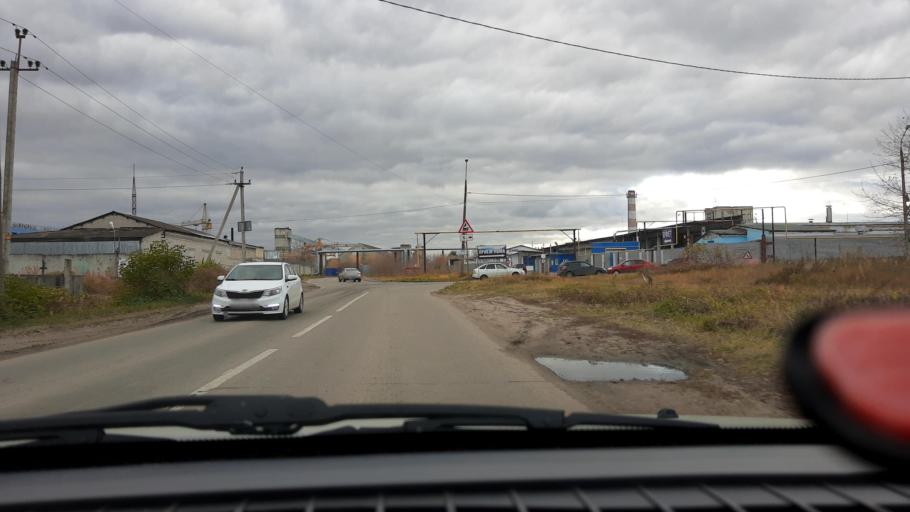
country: RU
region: Nizjnij Novgorod
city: Gorbatovka
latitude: 56.3457
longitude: 43.8247
